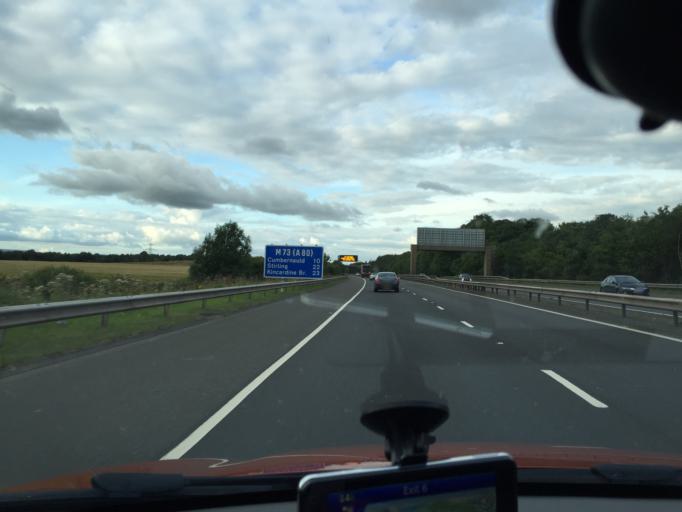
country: GB
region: Scotland
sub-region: South Lanarkshire
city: Uddingston
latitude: 55.8625
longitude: -4.0833
